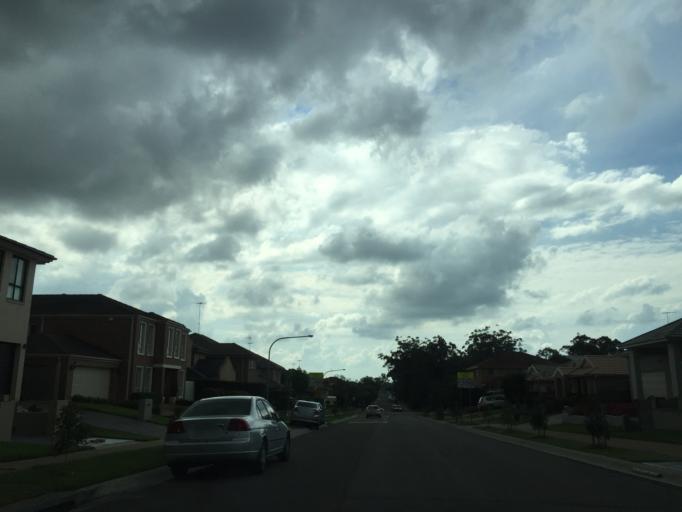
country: AU
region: New South Wales
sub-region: The Hills Shire
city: Beaumont Hills
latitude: -33.7105
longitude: 150.9673
